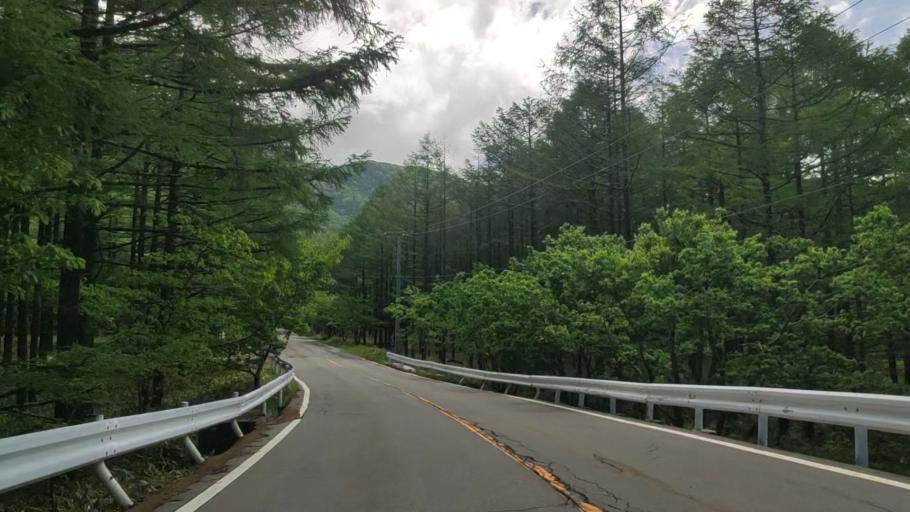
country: JP
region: Nagano
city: Chino
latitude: 36.0946
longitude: 138.2709
